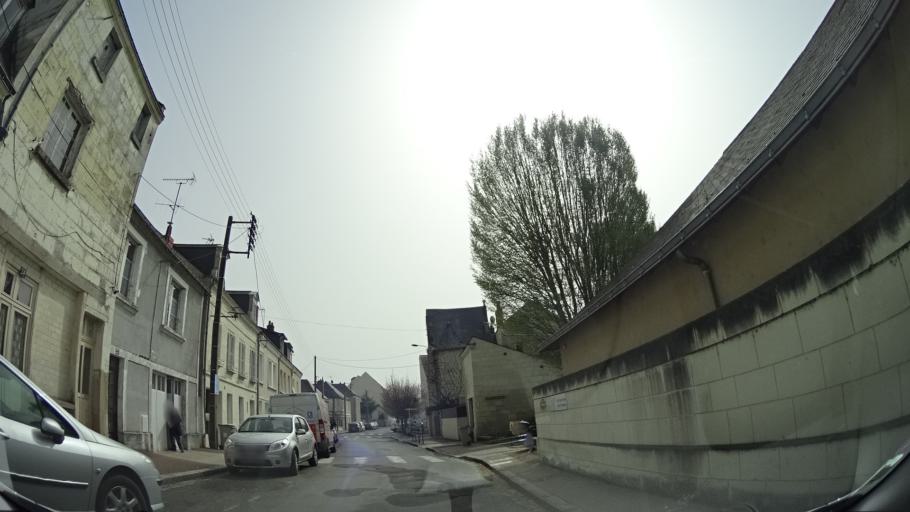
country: FR
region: Pays de la Loire
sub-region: Departement de Maine-et-Loire
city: Saumur
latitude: 47.2635
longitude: -0.0722
